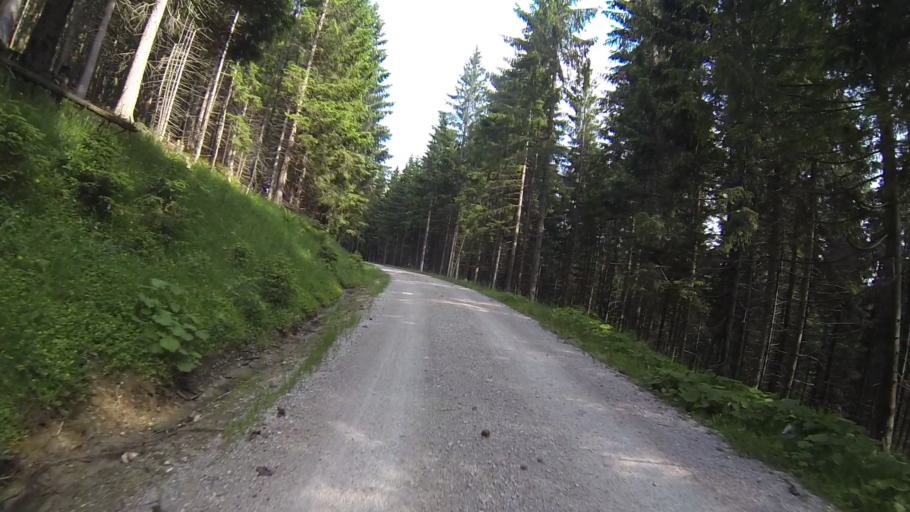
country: AT
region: Tyrol
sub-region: Politischer Bezirk Reutte
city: Jungholz
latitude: 47.5848
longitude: 10.4851
